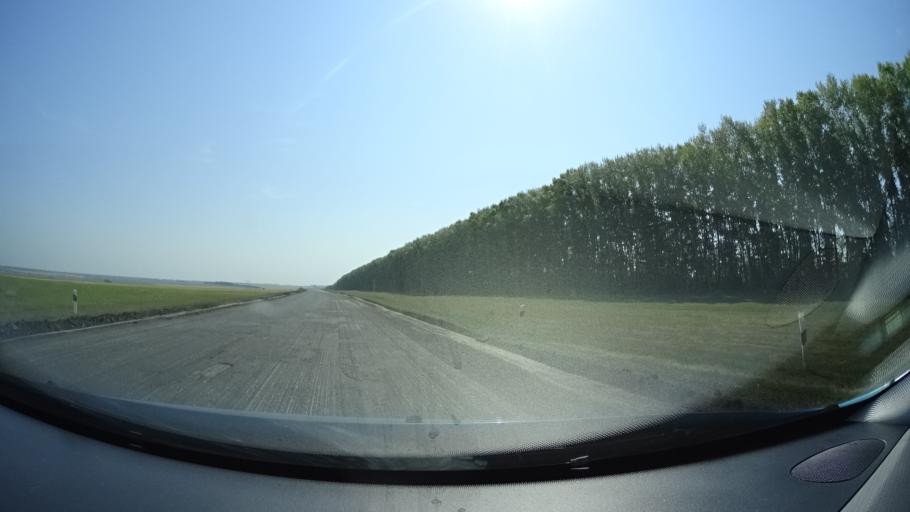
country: RU
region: Bashkortostan
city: Kabakovo
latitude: 54.4495
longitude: 55.9774
